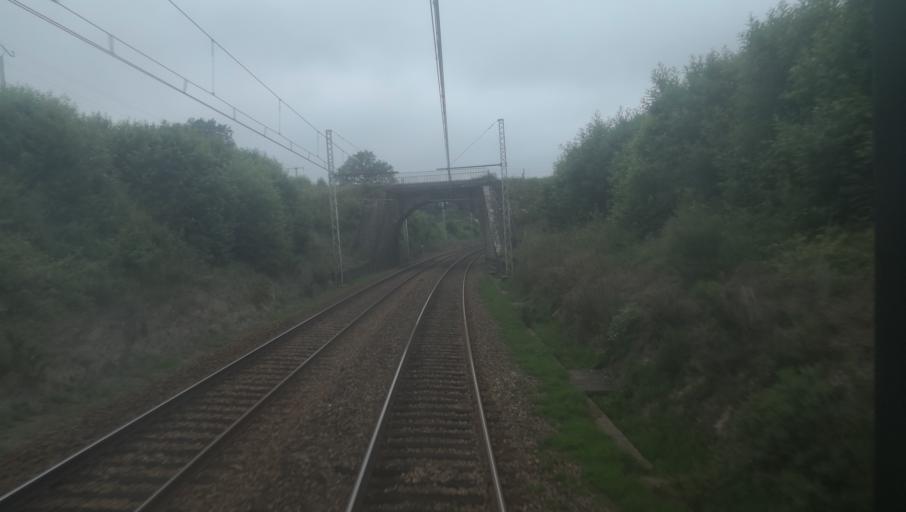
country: FR
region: Centre
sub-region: Departement de l'Indre
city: Chantome
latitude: 46.3696
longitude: 1.5371
